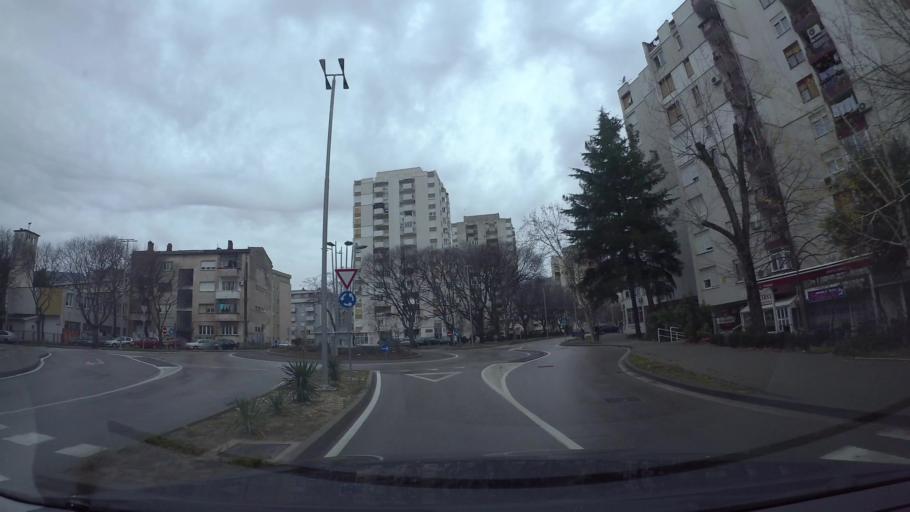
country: BA
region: Federation of Bosnia and Herzegovina
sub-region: Hercegovacko-Bosanski Kanton
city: Mostar
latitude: 43.3511
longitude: 17.8043
